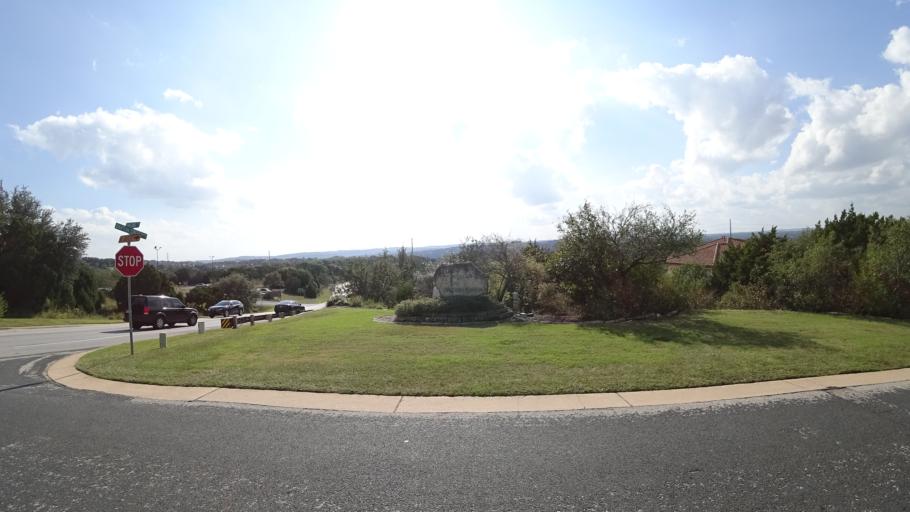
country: US
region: Texas
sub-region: Travis County
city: Lost Creek
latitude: 30.3035
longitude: -97.8438
